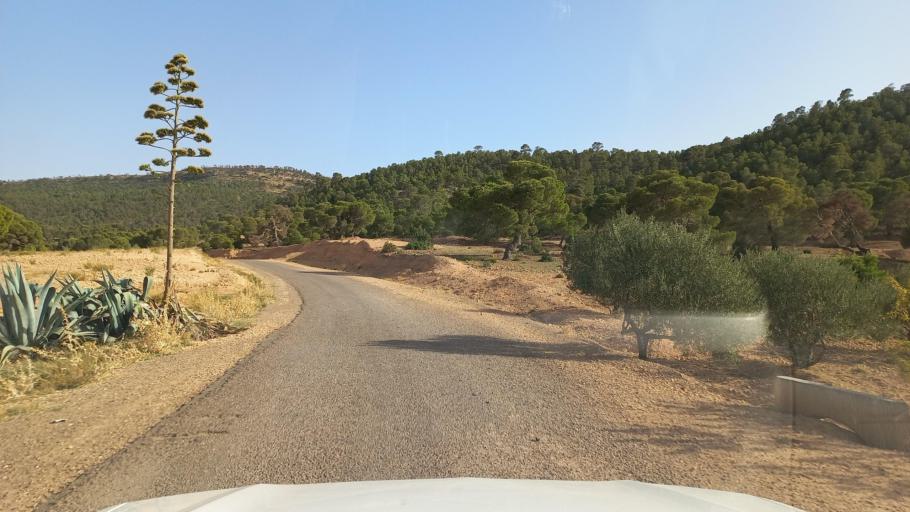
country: TN
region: Al Qasrayn
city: Kasserine
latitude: 35.3345
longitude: 8.8404
